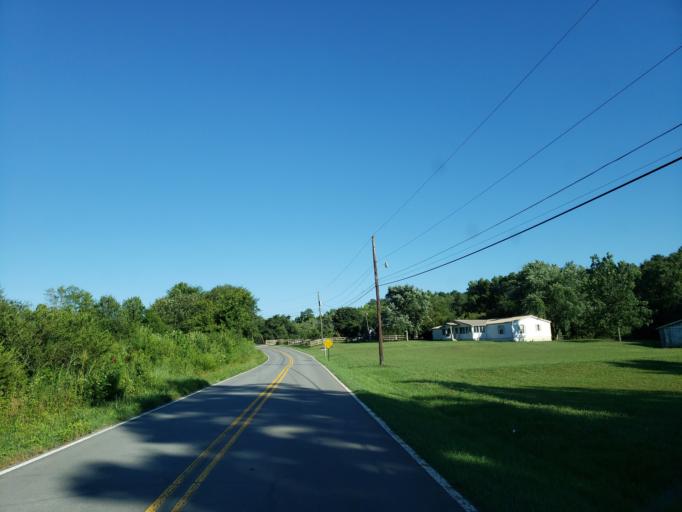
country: US
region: Georgia
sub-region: Bartow County
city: Euharlee
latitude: 34.0966
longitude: -84.9950
